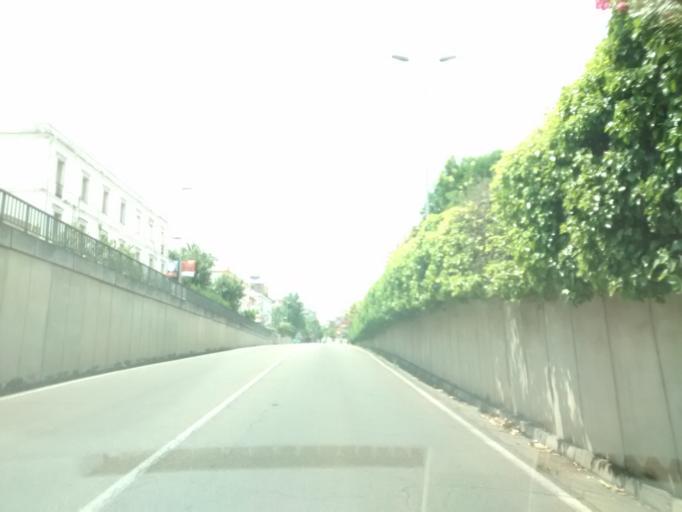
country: ES
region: Extremadura
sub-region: Provincia de Badajoz
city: Merida
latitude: 38.9200
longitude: -6.3367
